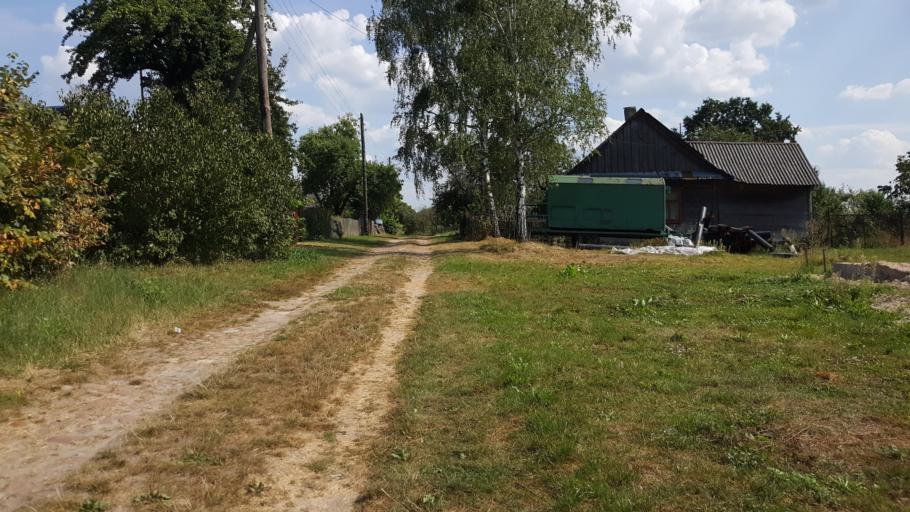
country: BY
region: Brest
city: Kamyanyuki
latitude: 52.5006
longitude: 23.6635
